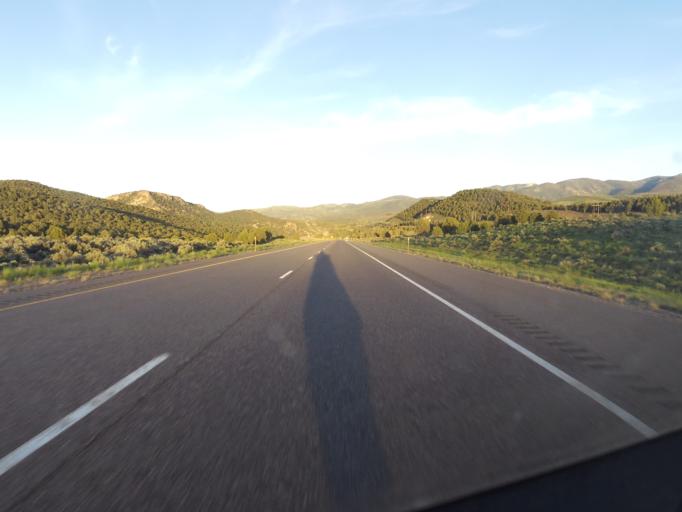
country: US
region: Utah
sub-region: Sevier County
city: Monroe
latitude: 38.5700
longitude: -112.4505
